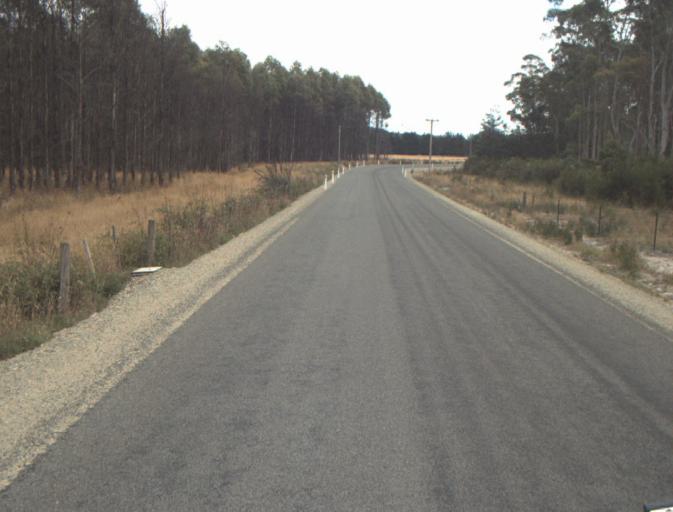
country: AU
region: Tasmania
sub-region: Launceston
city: Mayfield
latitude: -41.2149
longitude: 147.1920
